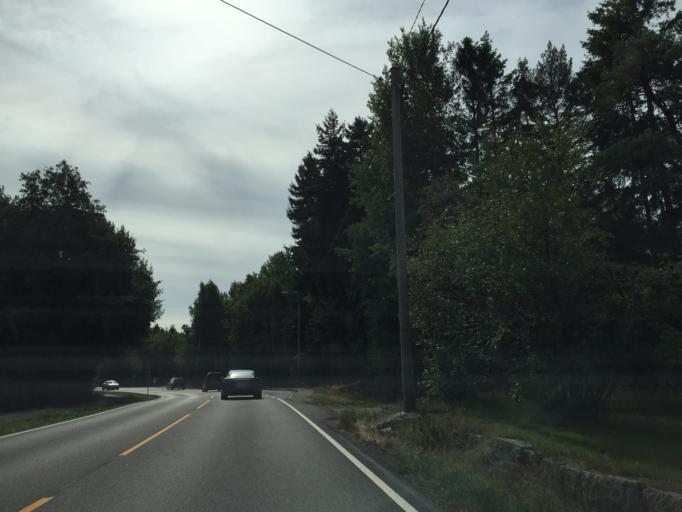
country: NO
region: Ostfold
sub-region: Fredrikstad
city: Fredrikstad
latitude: 59.1546
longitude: 10.9352
